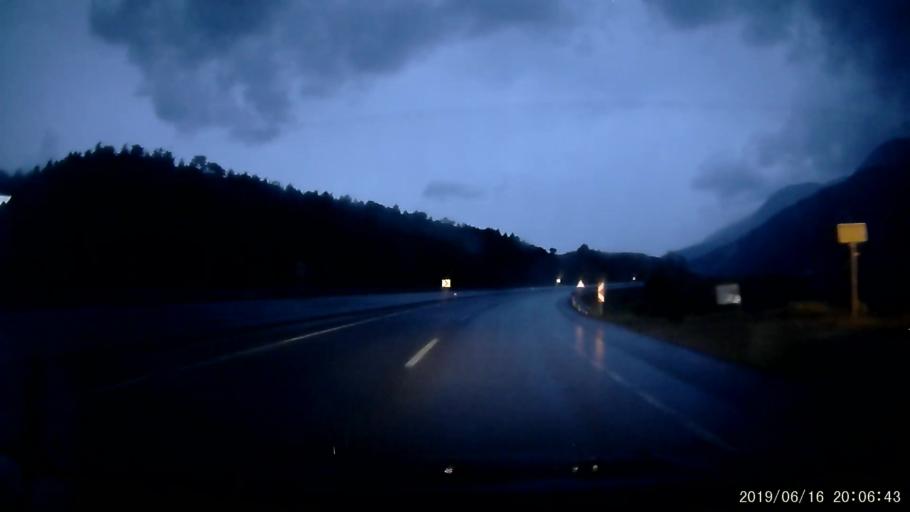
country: TR
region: Sivas
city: Dogansar
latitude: 40.3152
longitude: 37.6357
